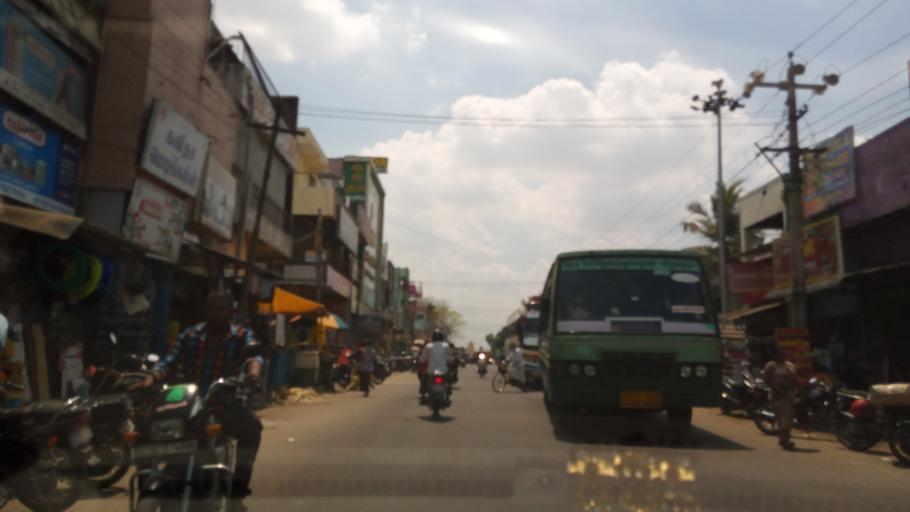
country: IN
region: Tamil Nadu
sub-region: Vellore
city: Walajapet
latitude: 12.9254
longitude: 79.3642
